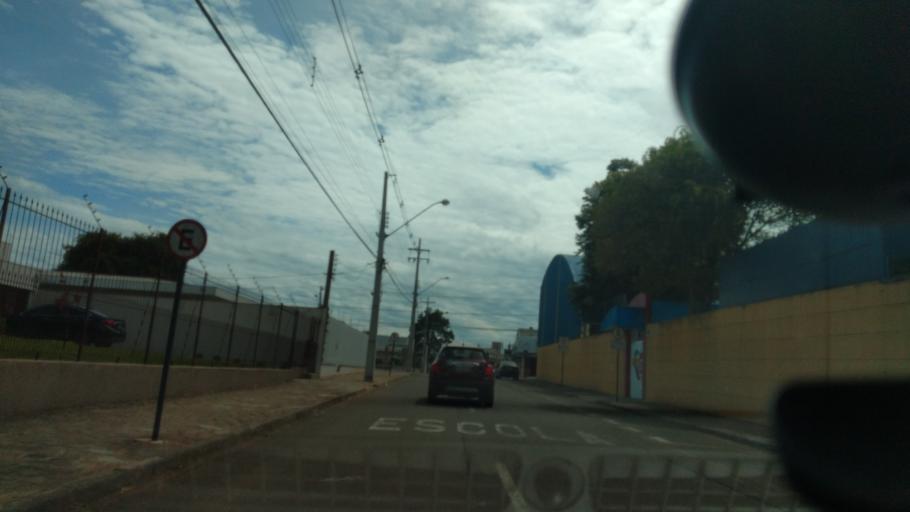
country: BR
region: Parana
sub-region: Guarapuava
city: Guarapuava
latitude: -25.3956
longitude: -51.4597
